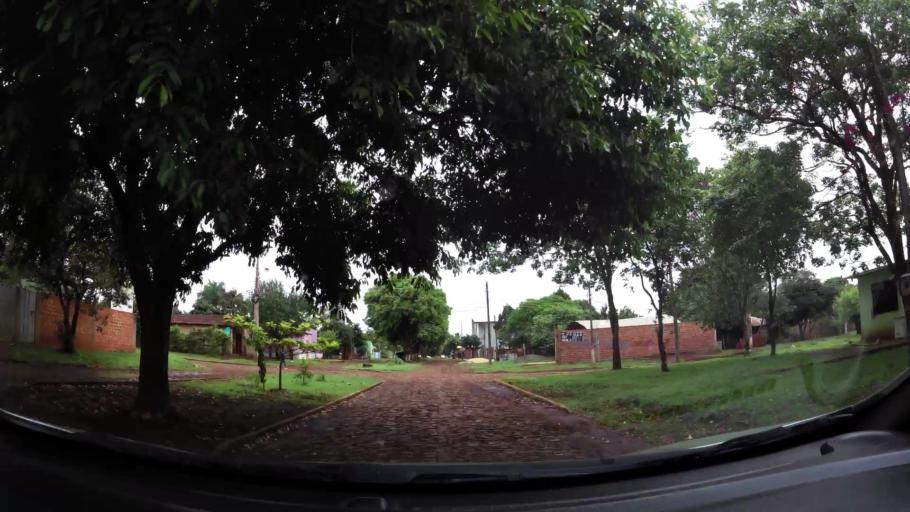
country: PY
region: Alto Parana
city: Ciudad del Este
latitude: -25.3746
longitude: -54.6509
